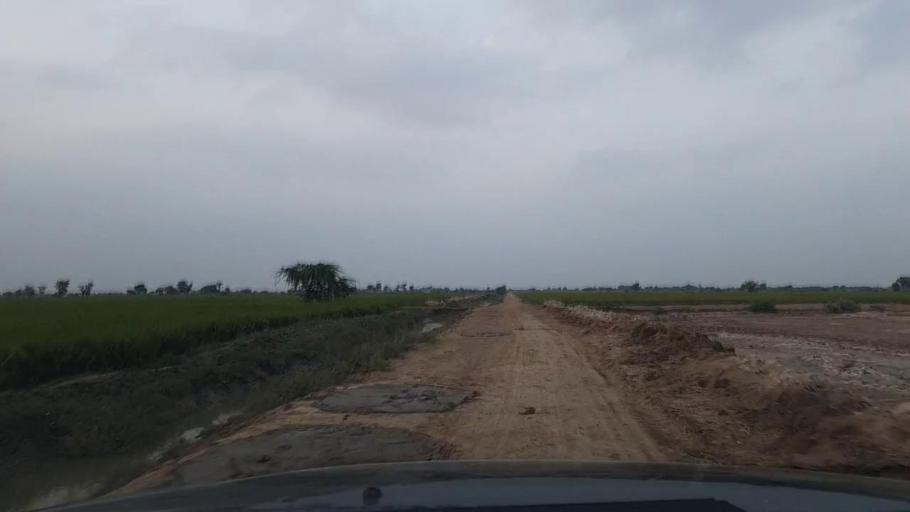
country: PK
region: Sindh
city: Jati
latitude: 24.5029
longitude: 68.3931
